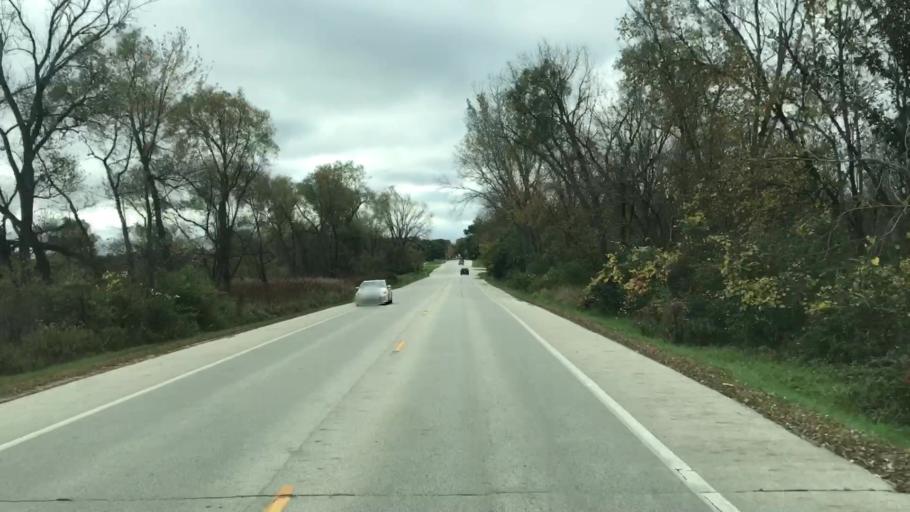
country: US
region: Wisconsin
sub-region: Waukesha County
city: Brookfield
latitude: 43.0743
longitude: -88.1258
